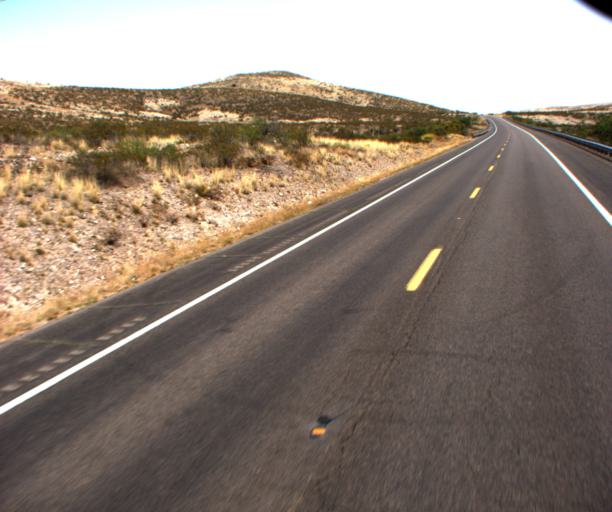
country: US
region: Arizona
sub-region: Greenlee County
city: Clifton
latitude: 32.7368
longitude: -109.1987
